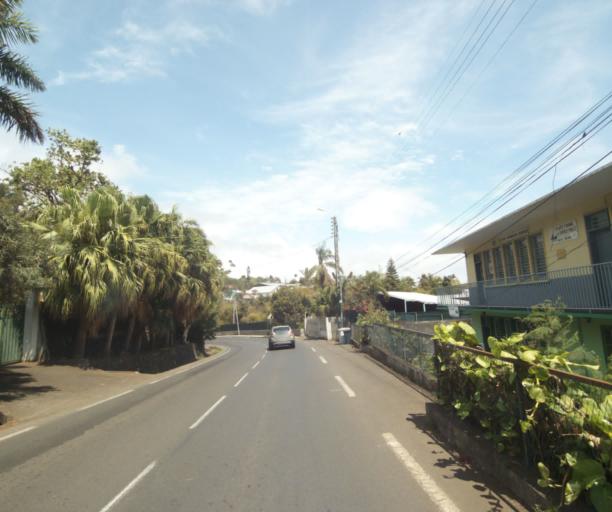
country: RE
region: Reunion
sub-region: Reunion
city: Trois-Bassins
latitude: -21.0824
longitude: 55.2702
